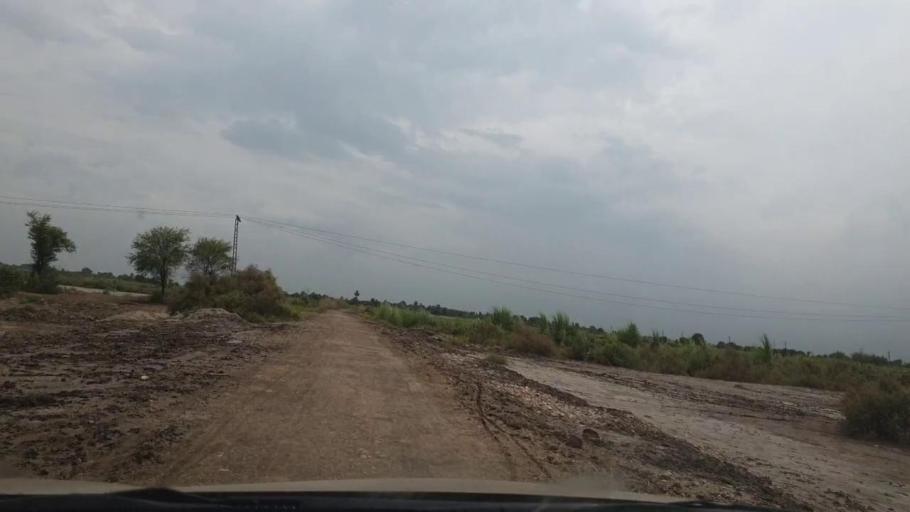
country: PK
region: Sindh
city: Ratodero
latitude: 27.8030
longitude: 68.3136
